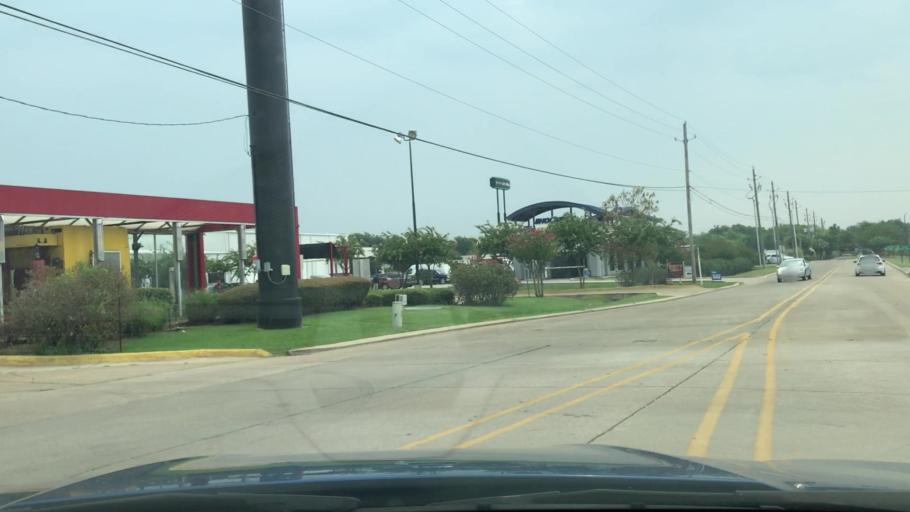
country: US
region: Louisiana
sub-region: Bossier Parish
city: Bossier City
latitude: 32.4198
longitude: -93.7211
